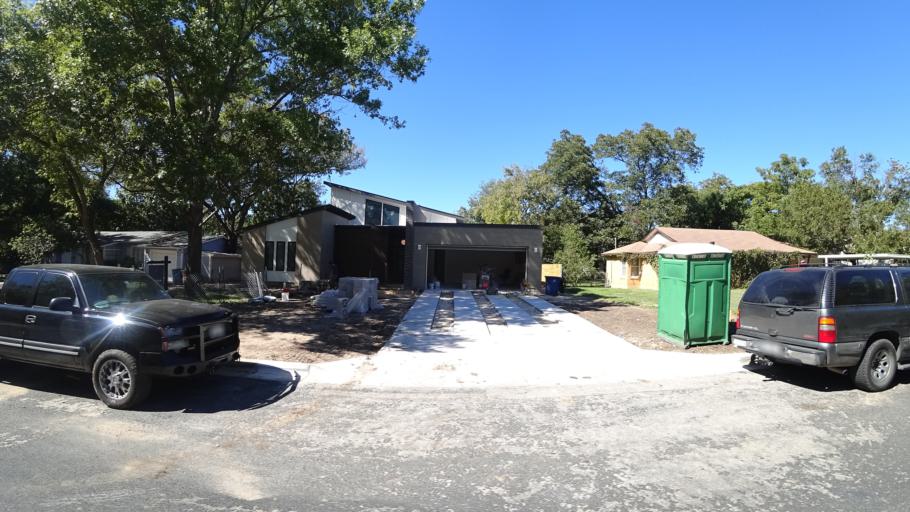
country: US
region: Texas
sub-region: Travis County
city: West Lake Hills
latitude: 30.3368
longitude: -97.7456
